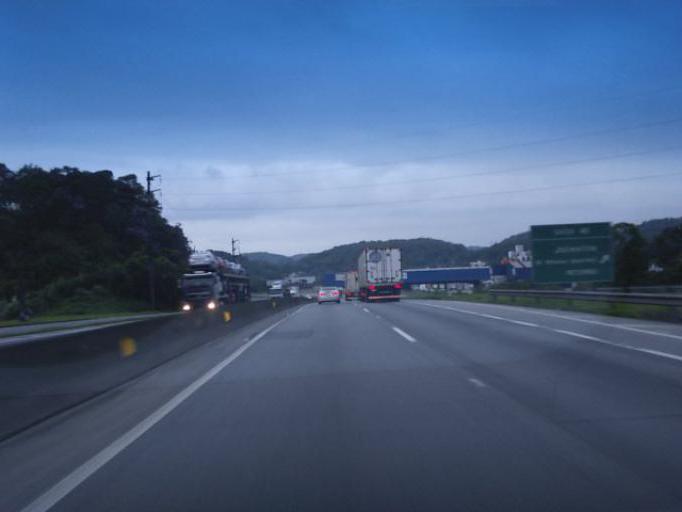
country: BR
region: Santa Catarina
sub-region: Joinville
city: Joinville
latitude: -26.3143
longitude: -48.8736
